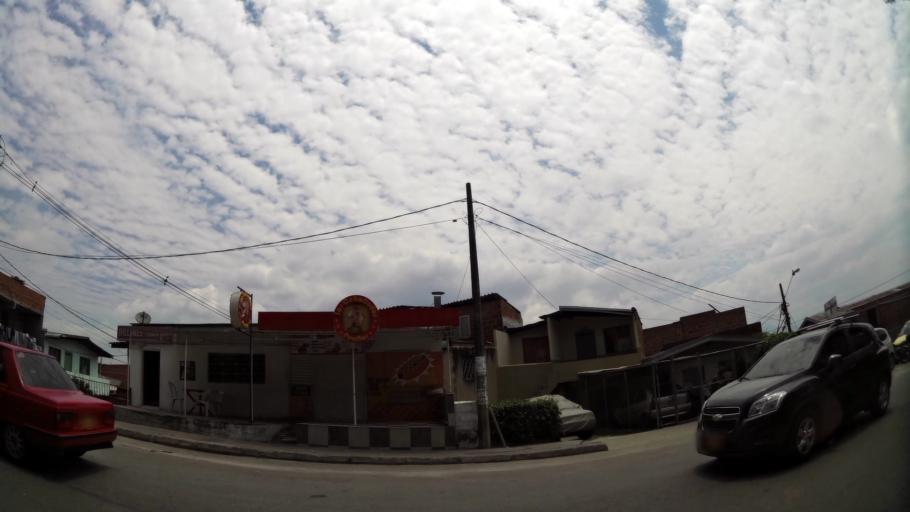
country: CO
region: Antioquia
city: Bello
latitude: 6.2991
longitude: -75.5822
